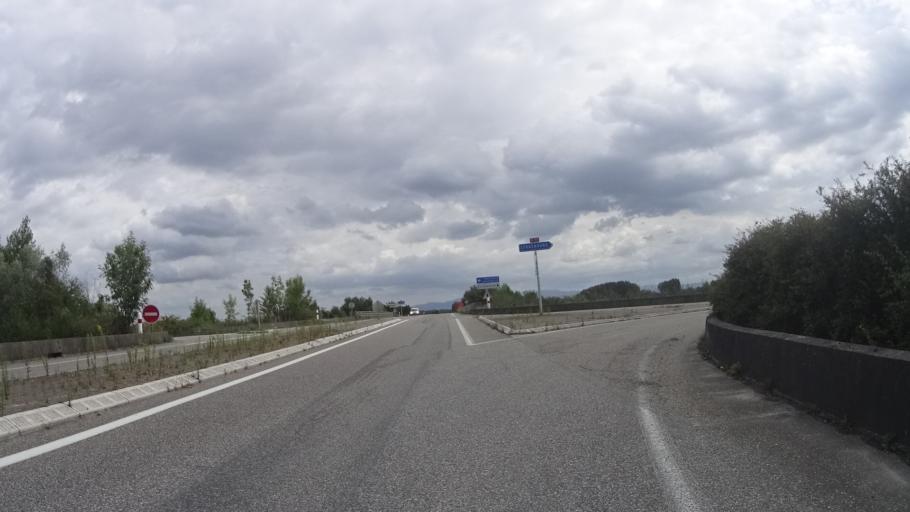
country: FR
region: Alsace
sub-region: Departement du Bas-Rhin
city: Kilstett
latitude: 48.7069
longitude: 7.8542
